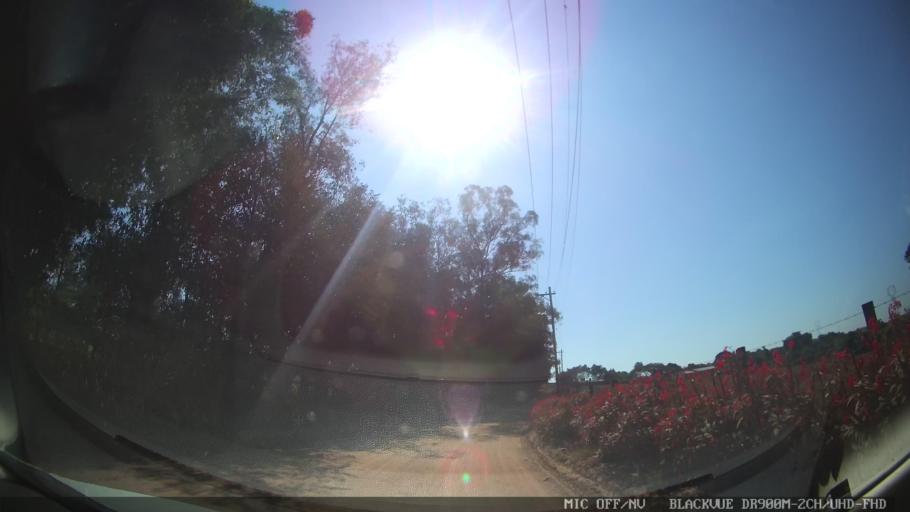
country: BR
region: Sao Paulo
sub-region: Itupeva
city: Itupeva
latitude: -23.1173
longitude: -47.0868
